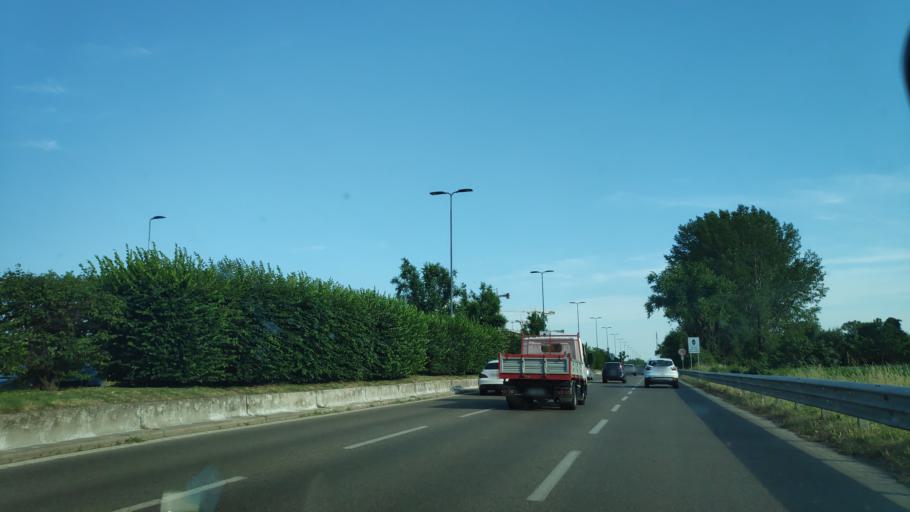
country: IT
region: Lombardy
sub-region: Citta metropolitana di Milano
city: Milano
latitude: 45.4290
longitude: 9.1954
